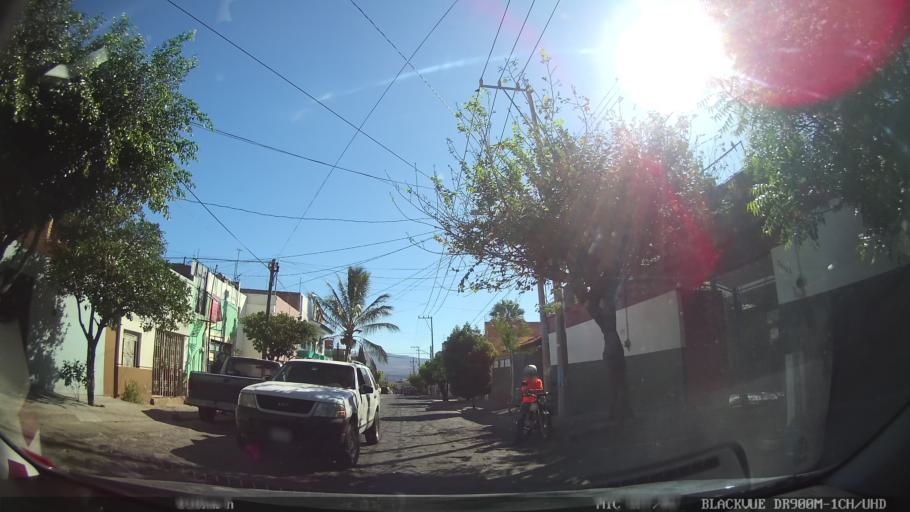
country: MX
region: Jalisco
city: Tlaquepaque
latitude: 20.6864
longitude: -103.2783
